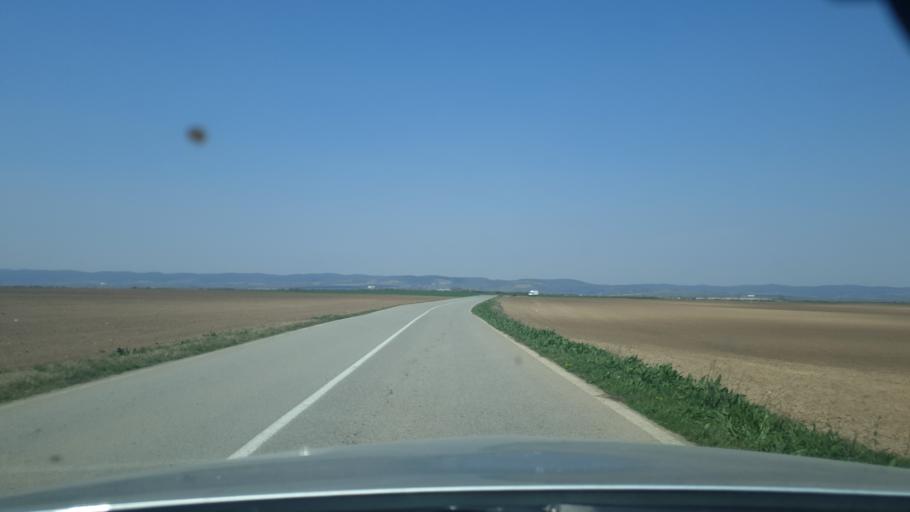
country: RS
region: Autonomna Pokrajina Vojvodina
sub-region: Sremski Okrug
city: Ruma
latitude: 45.0411
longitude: 19.7610
